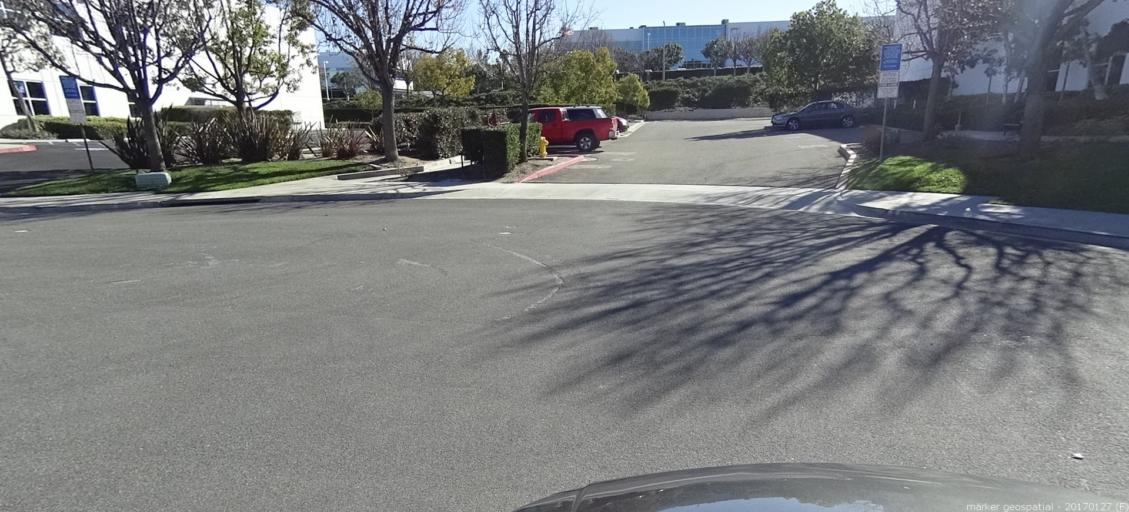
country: US
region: California
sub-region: Orange County
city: Foothill Ranch
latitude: 33.6672
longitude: -117.6610
